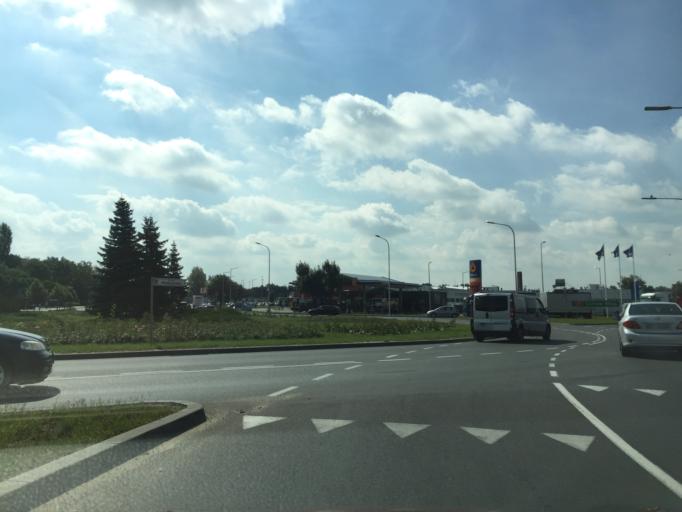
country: PL
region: Greater Poland Voivodeship
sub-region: Kalisz
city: Kalisz
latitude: 51.7490
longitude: 18.0631
